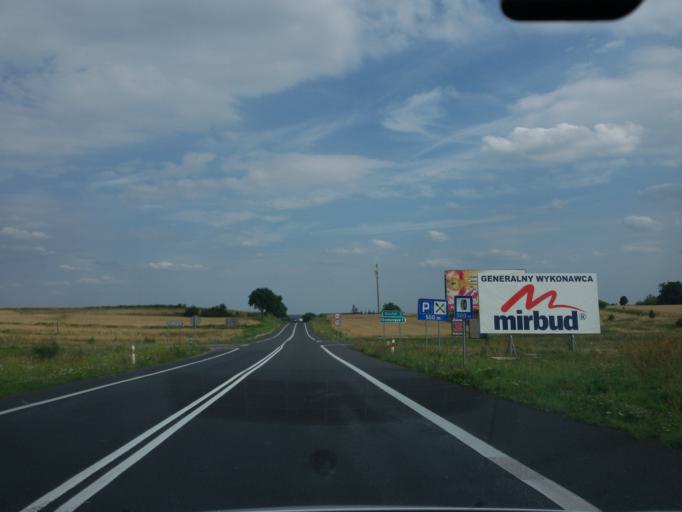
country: PL
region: Lower Silesian Voivodeship
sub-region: Powiat polkowicki
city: Gaworzyce
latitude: 51.6373
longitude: 15.8892
